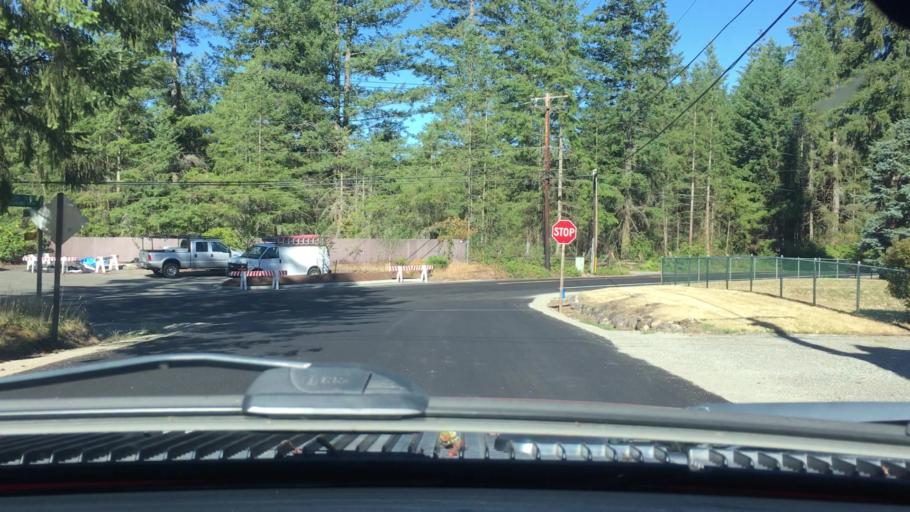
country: US
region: Washington
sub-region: King County
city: Lake Morton-Berrydale
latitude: 47.3175
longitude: -122.1013
